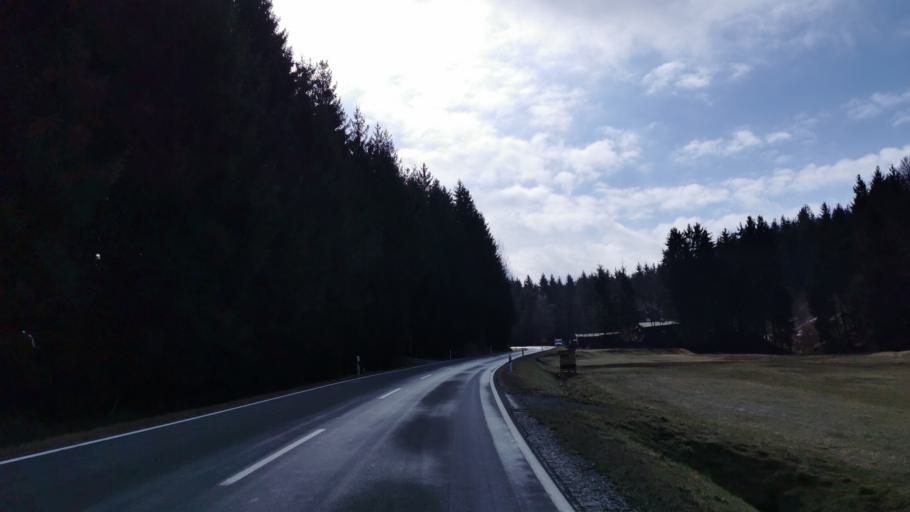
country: DE
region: Bavaria
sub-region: Upper Franconia
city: Reichenbach
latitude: 50.4276
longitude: 11.3998
